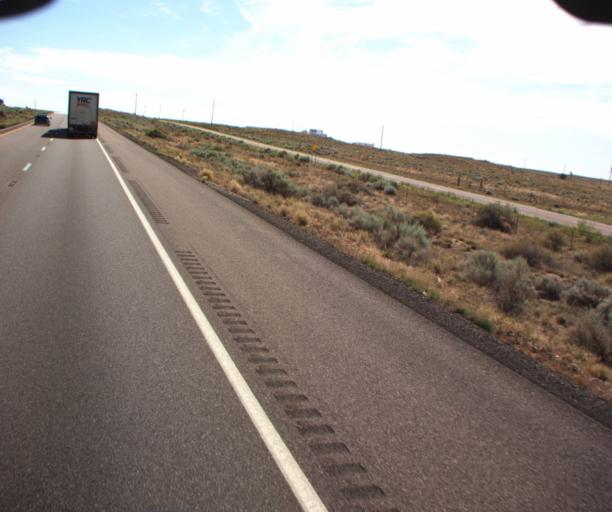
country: US
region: Arizona
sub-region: Navajo County
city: Holbrook
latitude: 35.0045
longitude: -109.8828
